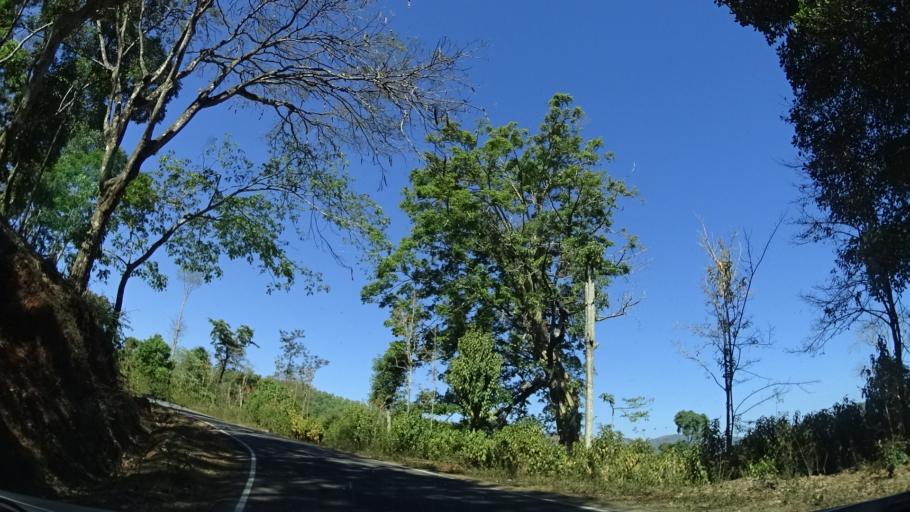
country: IN
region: Karnataka
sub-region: Chikmagalur
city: Sringeri
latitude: 13.2359
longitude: 75.3757
